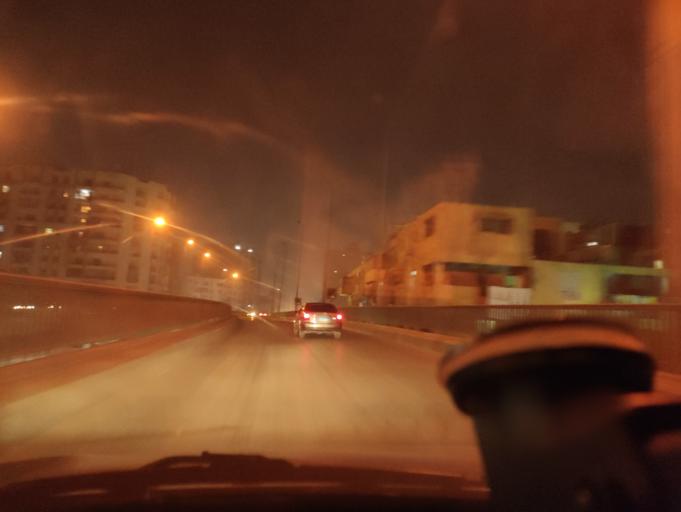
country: EG
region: Muhafazat al Qahirah
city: Cairo
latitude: 30.0935
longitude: 31.2742
